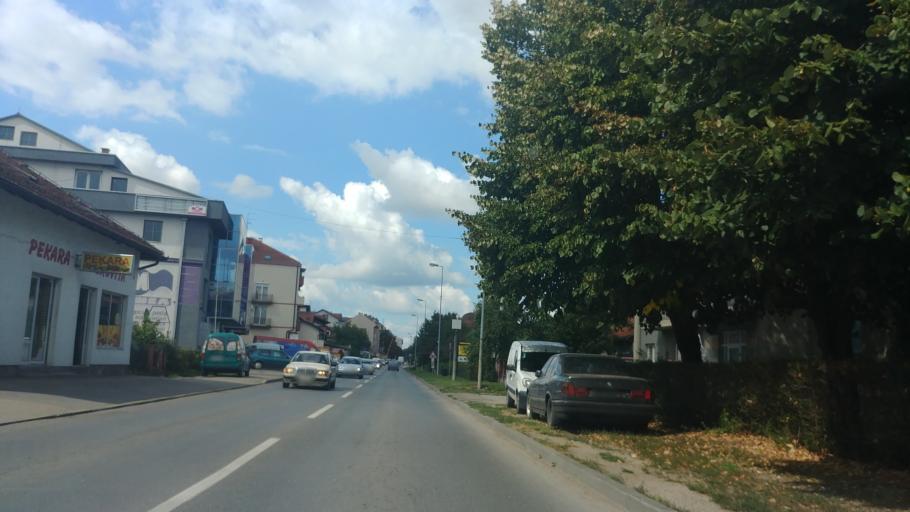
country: BA
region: Brcko
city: Brcko
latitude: 44.8676
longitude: 18.8189
